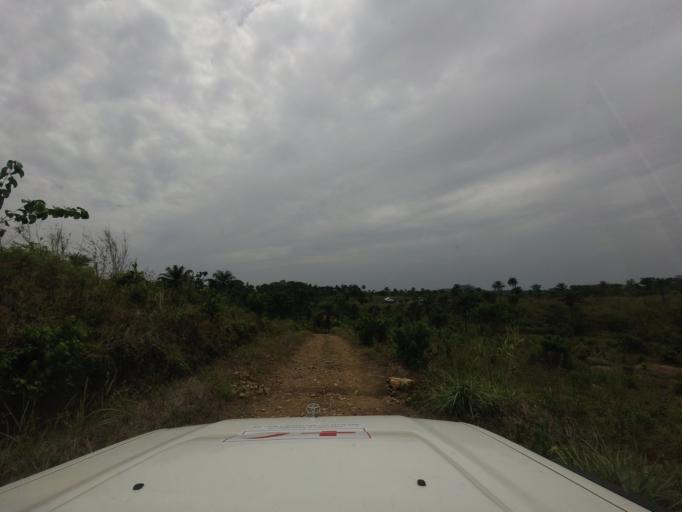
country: SL
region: Eastern Province
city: Buedu
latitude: 8.4260
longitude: -10.2604
